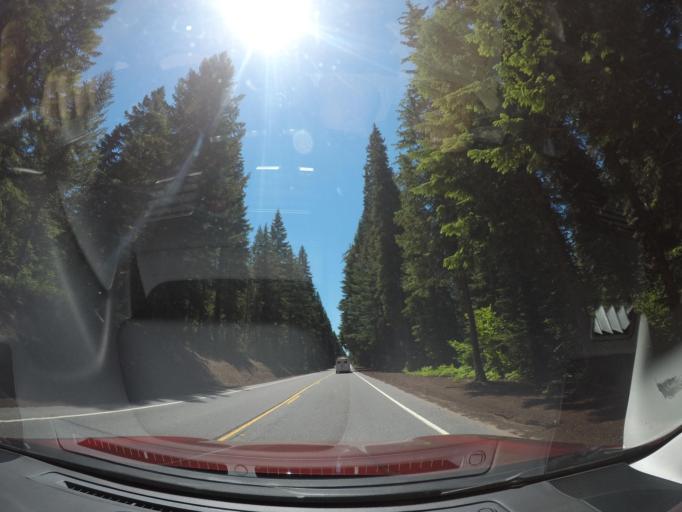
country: US
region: Oregon
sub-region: Deschutes County
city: Sisters
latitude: 44.5381
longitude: -121.9950
